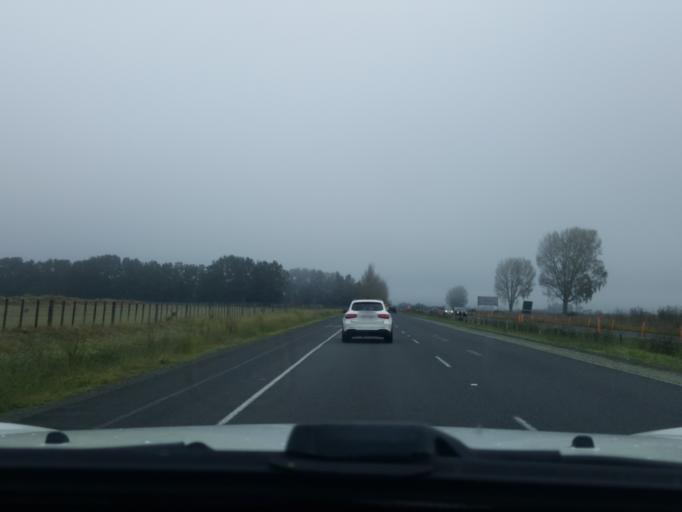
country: NZ
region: Waikato
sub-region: Waikato District
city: Te Kauwhata
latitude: -37.5005
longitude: 175.1641
